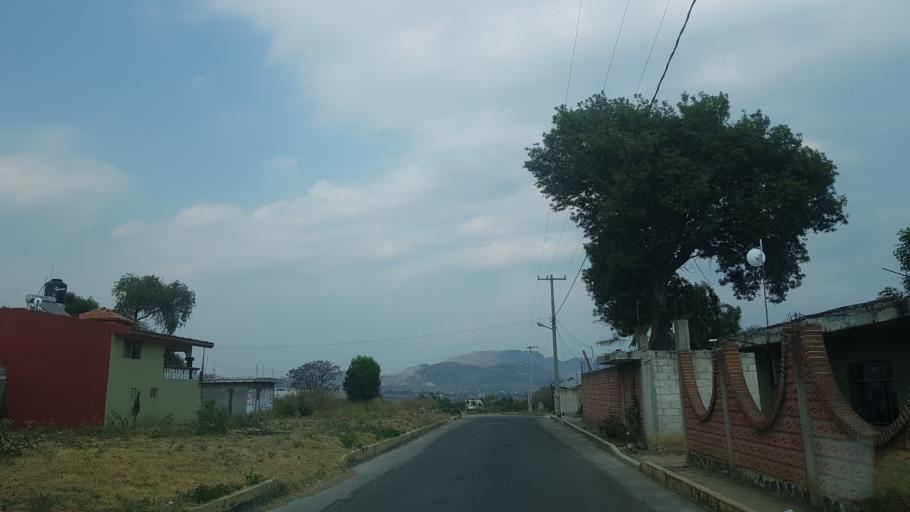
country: MX
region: Puebla
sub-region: Santa Isabel Cholula
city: San Martin Tlamapa
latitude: 18.9597
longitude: -98.4061
